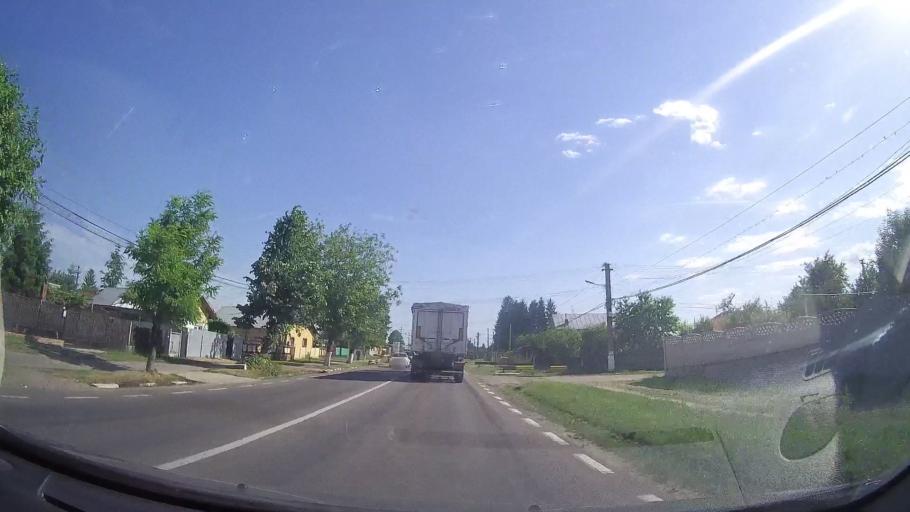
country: RO
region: Prahova
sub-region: Comuna Lipanesti
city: Lipanesti
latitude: 45.0571
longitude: 26.0203
